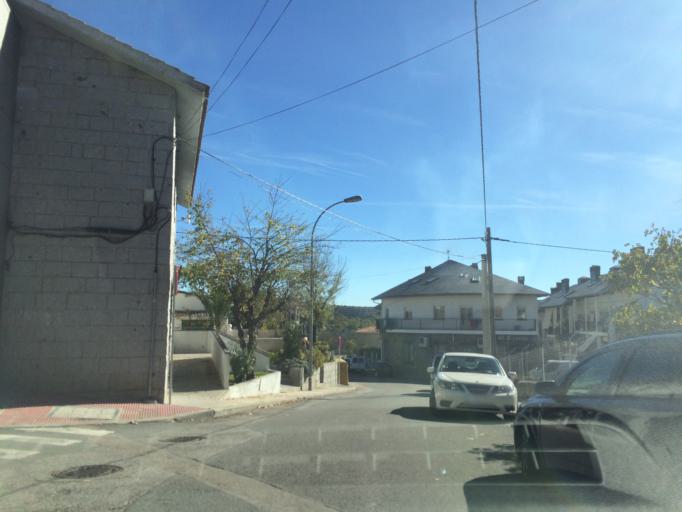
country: ES
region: Madrid
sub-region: Provincia de Madrid
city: Boalo
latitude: 40.7188
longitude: -3.9185
